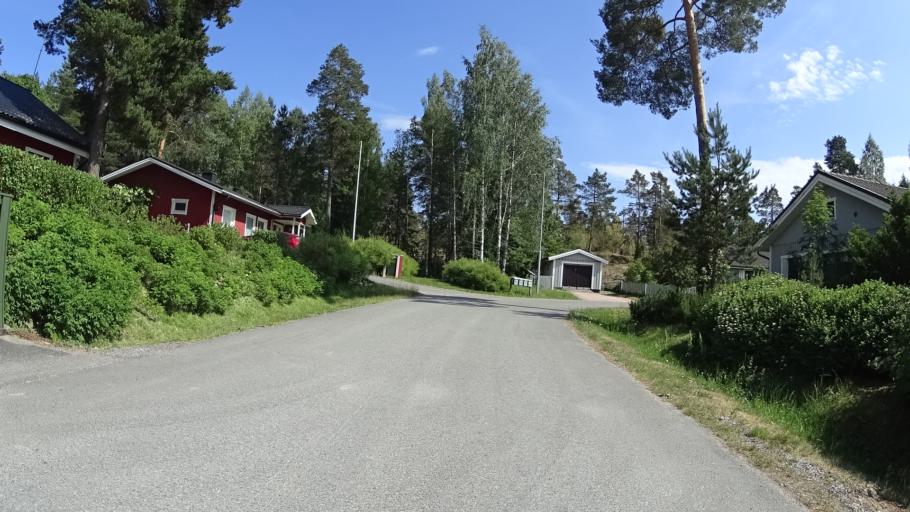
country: FI
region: Uusimaa
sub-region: Raaseporin
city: Karis
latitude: 60.0862
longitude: 23.6523
